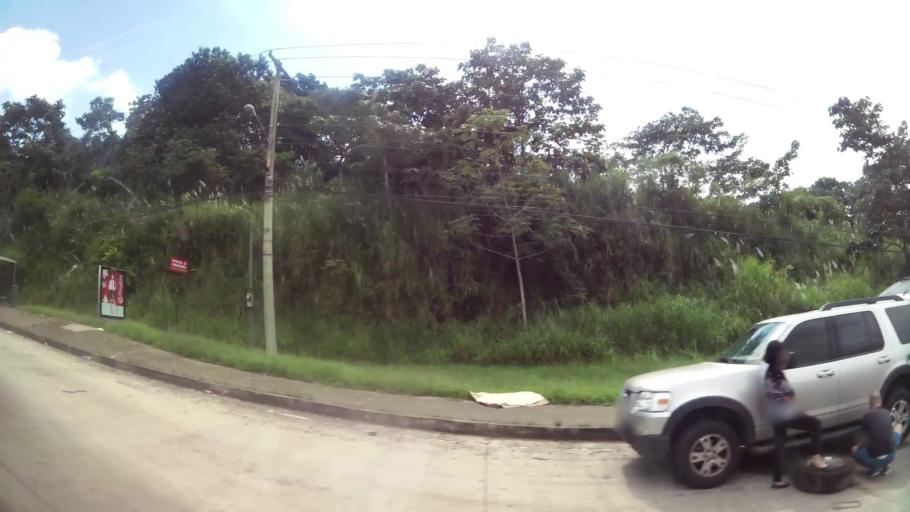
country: PA
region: Panama
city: Panama
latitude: 9.0391
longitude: -79.5454
